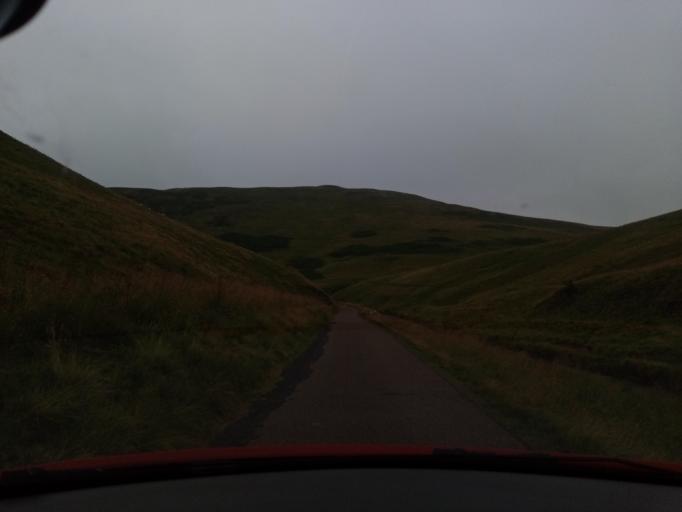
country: GB
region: England
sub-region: Northumberland
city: Rochester
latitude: 55.3914
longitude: -2.2343
